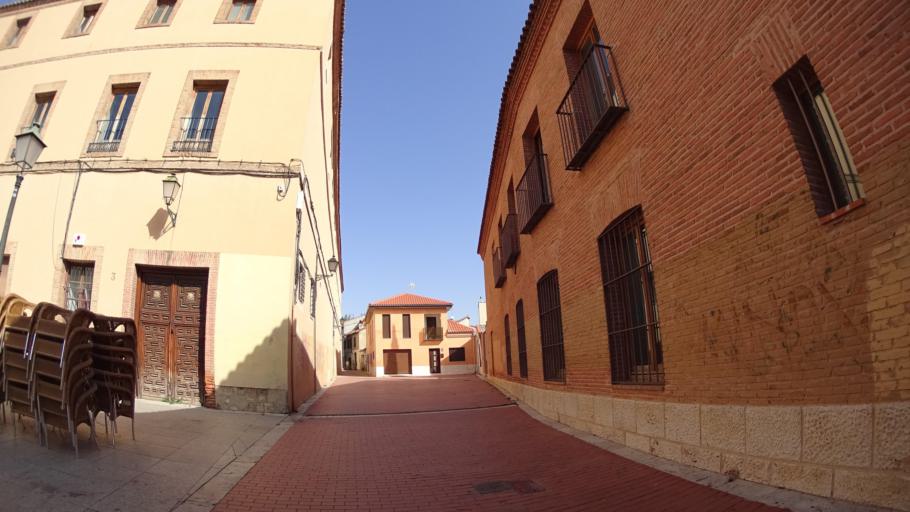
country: ES
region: Madrid
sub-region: Provincia de Madrid
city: Alcala de Henares
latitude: 40.4799
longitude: -3.3704
